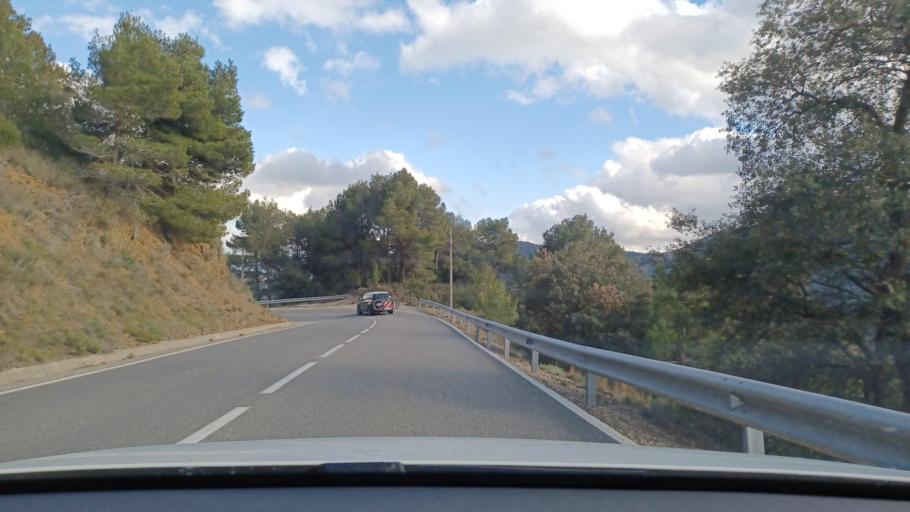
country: ES
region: Catalonia
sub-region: Provincia de Tarragona
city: Alforja
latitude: 41.2199
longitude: 0.9477
